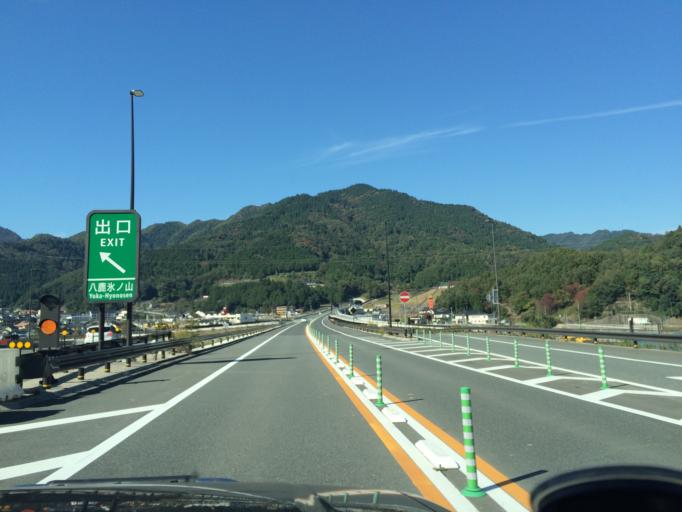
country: JP
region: Hyogo
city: Toyooka
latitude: 35.3897
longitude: 134.7490
